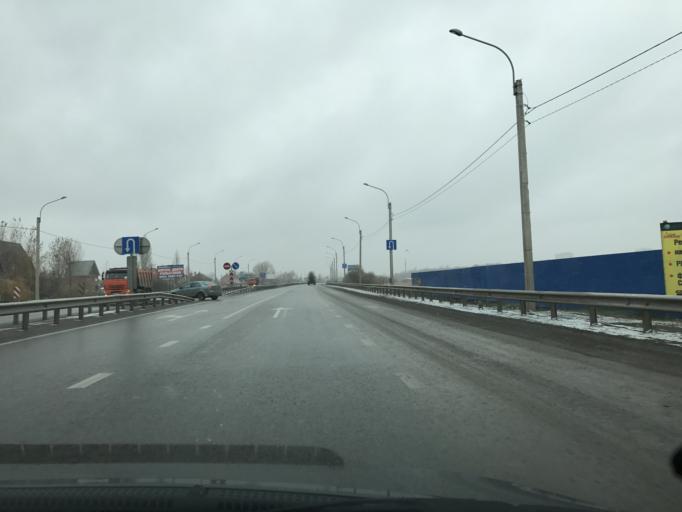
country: RU
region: Rostov
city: Bataysk
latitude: 47.1528
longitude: 39.7713
